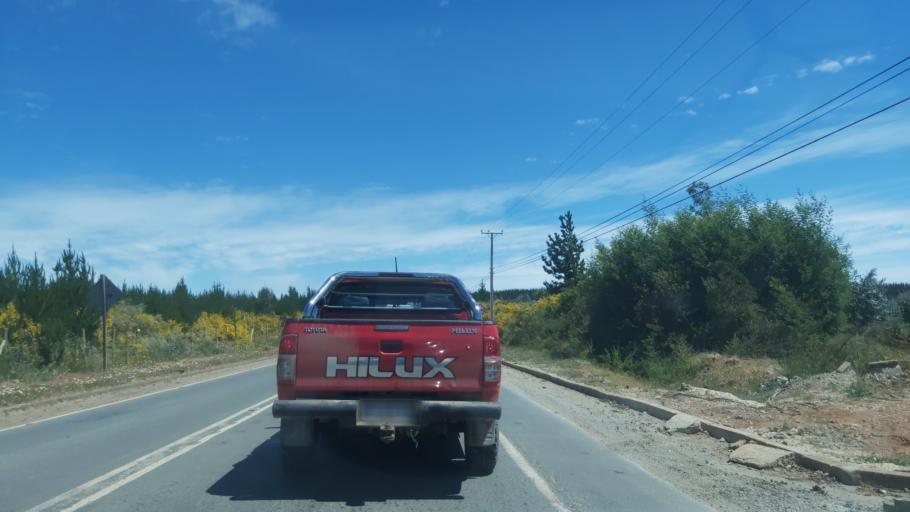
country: CL
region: Maule
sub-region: Provincia de Talca
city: Constitucion
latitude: -35.4050
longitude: -72.4379
